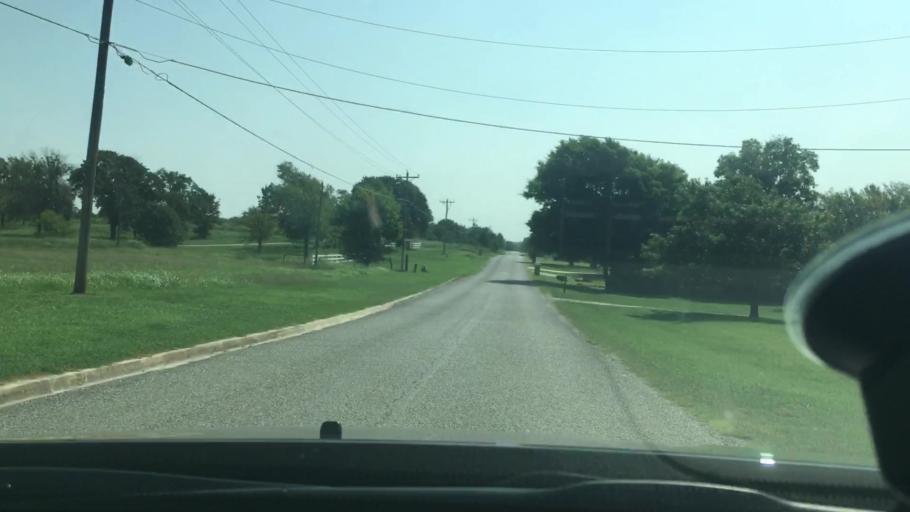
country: US
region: Oklahoma
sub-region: Bryan County
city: Durant
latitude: 34.0121
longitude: -96.4395
